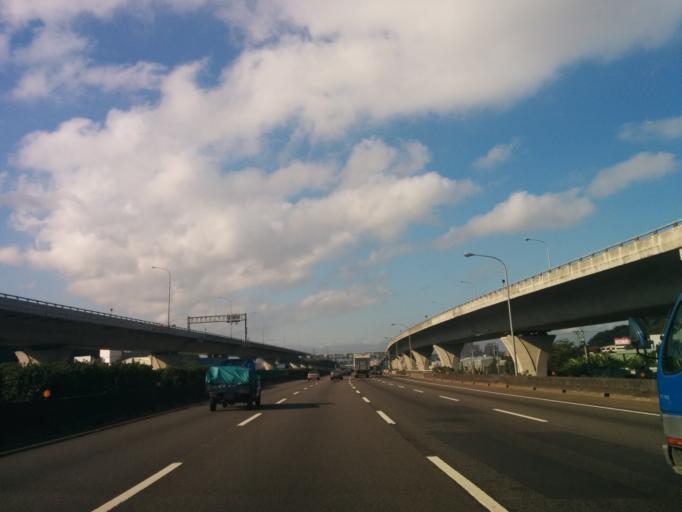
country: TW
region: Taiwan
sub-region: Taoyuan
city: Taoyuan
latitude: 25.0483
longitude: 121.3202
